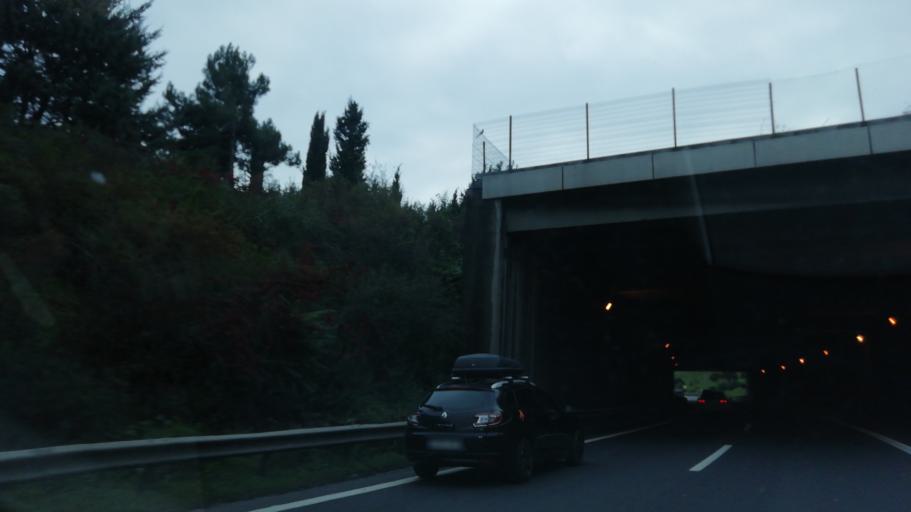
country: TR
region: Istanbul
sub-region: Atasehir
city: Atasehir
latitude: 40.9961
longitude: 29.1223
